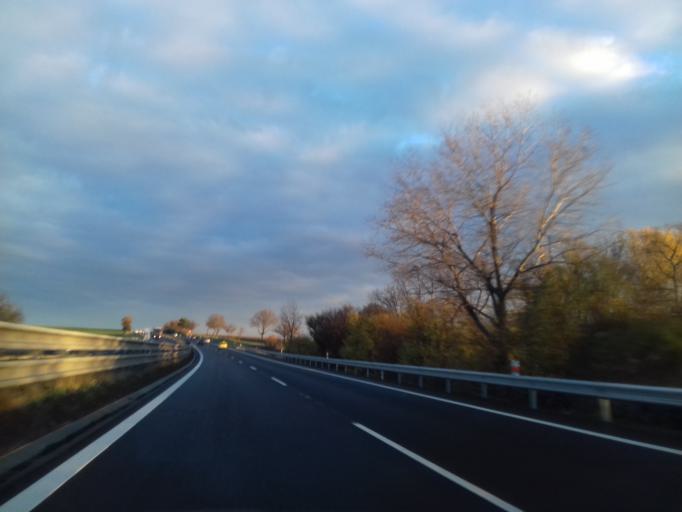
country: CZ
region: Olomoucky
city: Urcice
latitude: 49.4133
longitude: 17.1113
